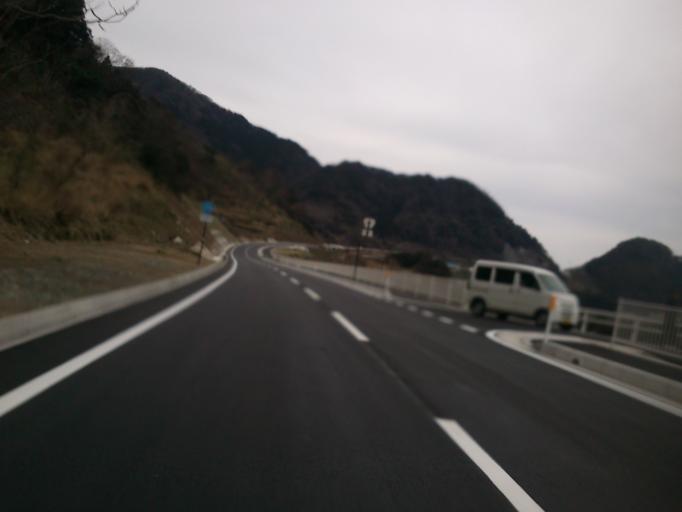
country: JP
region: Kyoto
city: Miyazu
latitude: 35.7456
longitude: 135.2553
